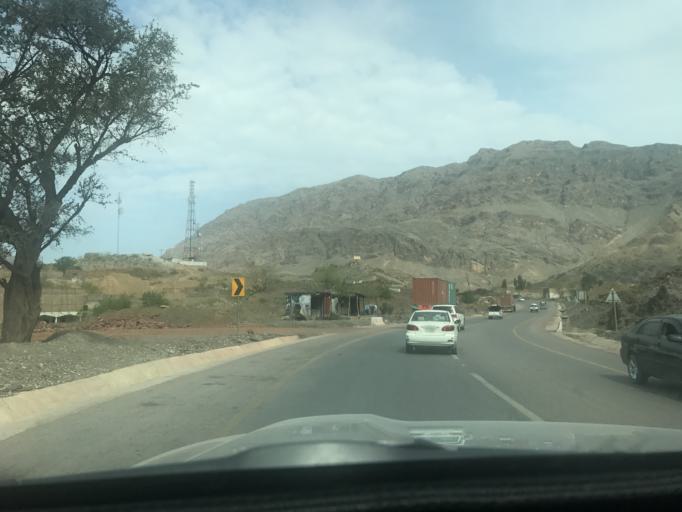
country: PK
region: Federally Administered Tribal Areas
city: Landi Kotal
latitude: 34.0100
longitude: 71.2868
